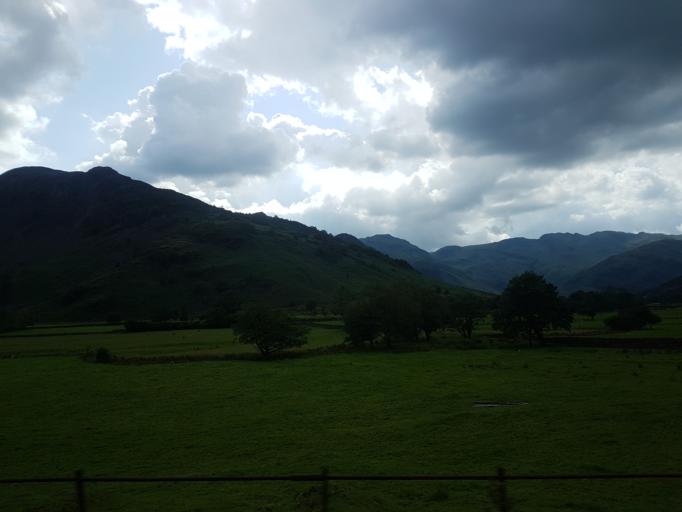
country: GB
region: England
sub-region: Cumbria
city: Ambleside
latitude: 54.4489
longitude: -3.0684
